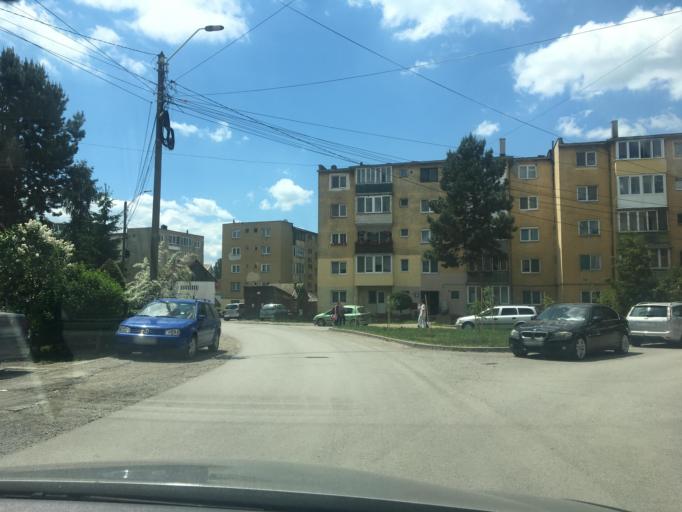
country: RO
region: Harghita
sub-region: Municipiul Gheorgheni
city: Gheorgheni
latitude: 46.7211
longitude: 25.5922
